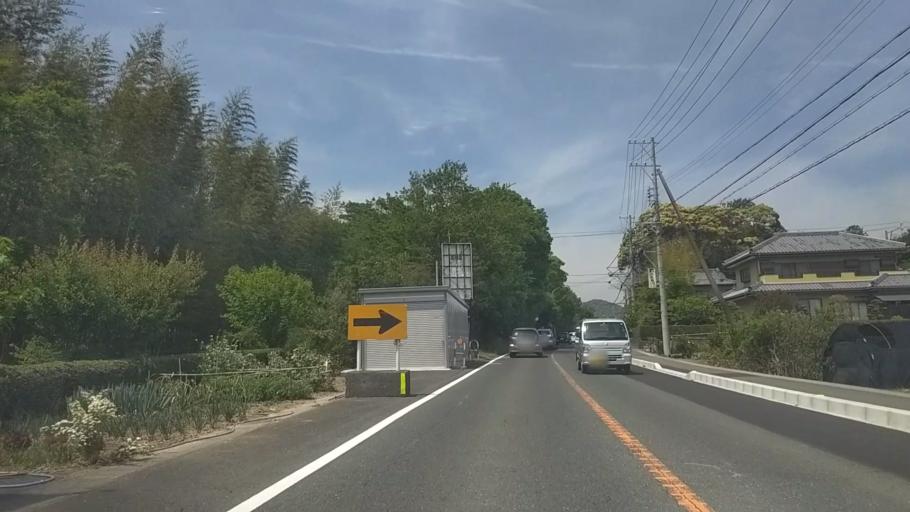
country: JP
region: Shizuoka
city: Kosai-shi
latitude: 34.7437
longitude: 137.5145
